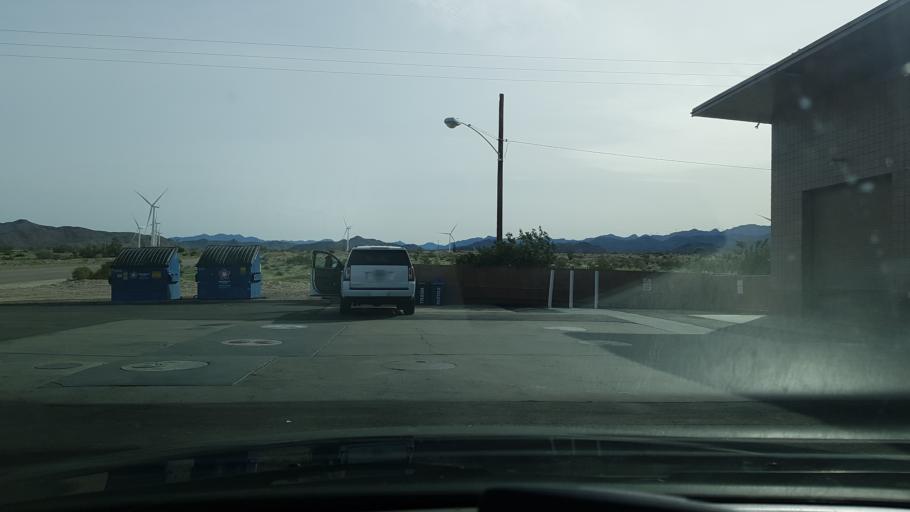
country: US
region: California
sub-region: Imperial County
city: Seeley
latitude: 32.7308
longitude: -115.9945
